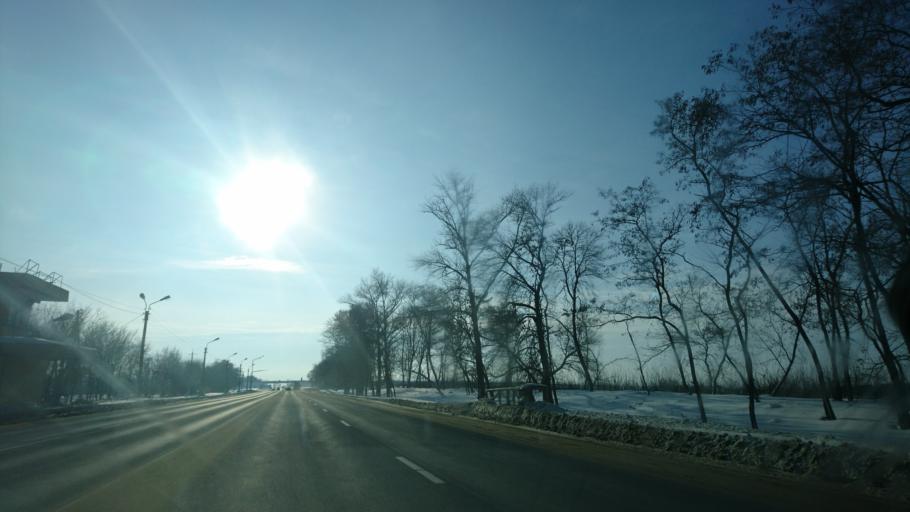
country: RU
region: Belgorod
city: Severnyy
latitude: 50.7301
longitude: 36.5295
